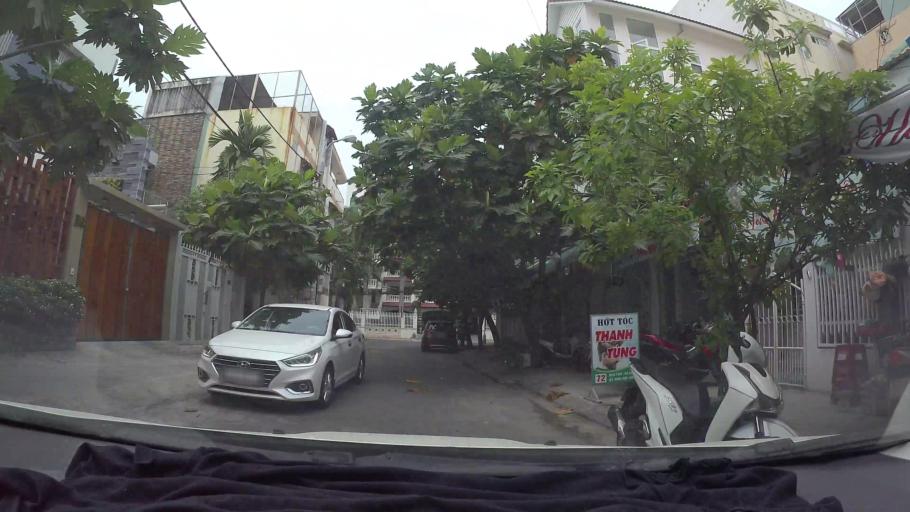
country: VN
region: Da Nang
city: Da Nang
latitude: 16.0563
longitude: 108.2208
